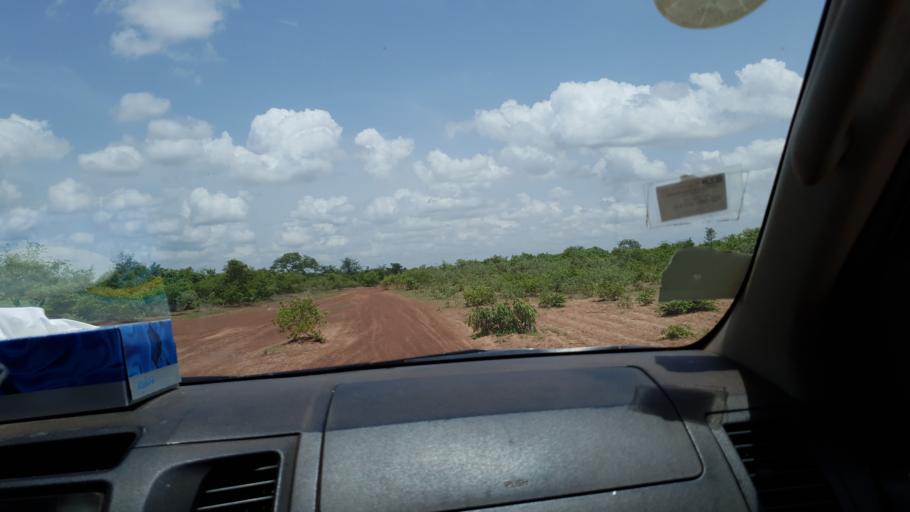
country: ML
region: Koulikoro
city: Banamba
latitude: 13.3783
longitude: -7.2081
